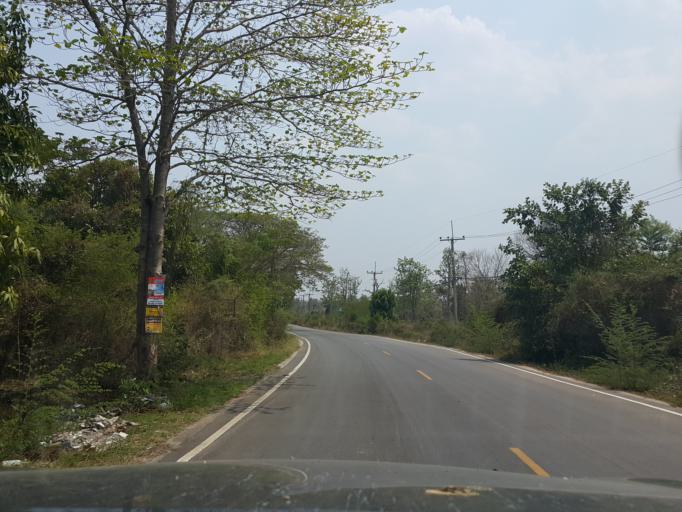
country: TH
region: Lampang
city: Mae Phrik
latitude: 17.4946
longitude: 99.1256
